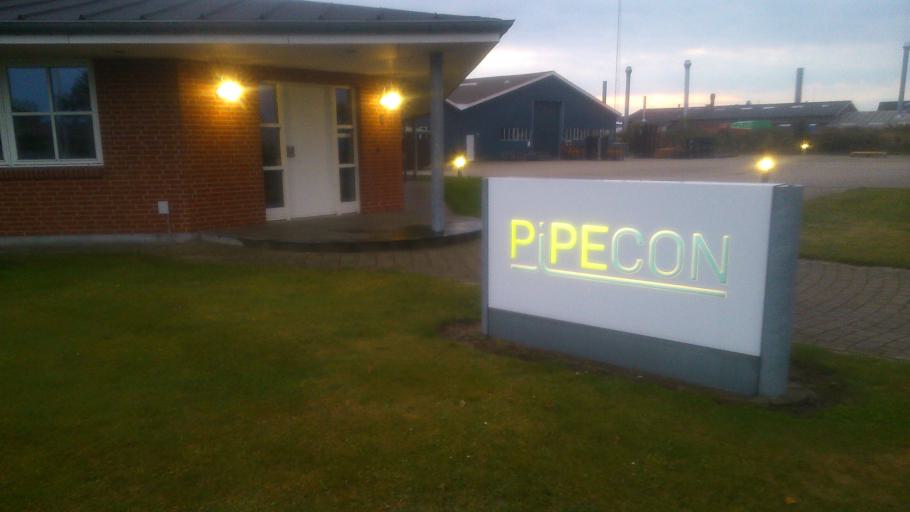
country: DK
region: Central Jutland
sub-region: Ringkobing-Skjern Kommune
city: Skjern
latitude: 55.9610
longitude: 8.4970
